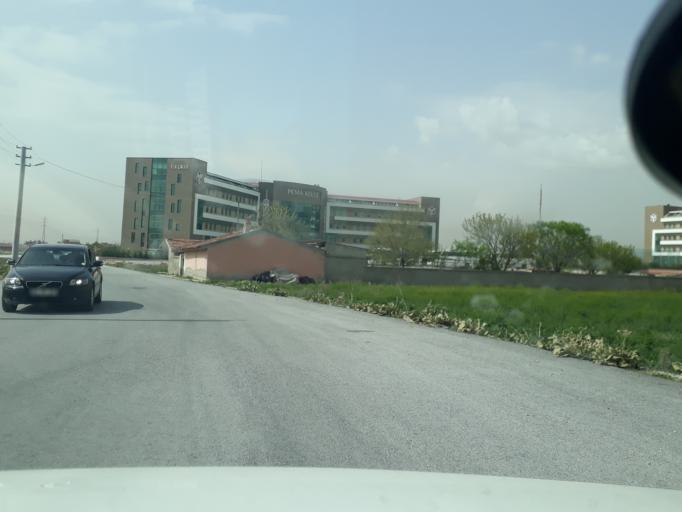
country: TR
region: Konya
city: Sille
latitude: 37.9474
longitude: 32.4757
